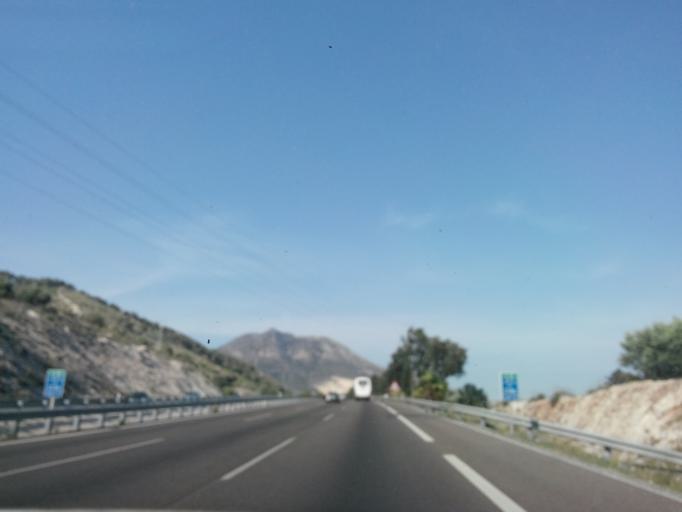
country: ES
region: Andalusia
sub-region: Provincia de Malaga
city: Benalmadena
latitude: 36.5935
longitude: -4.5792
